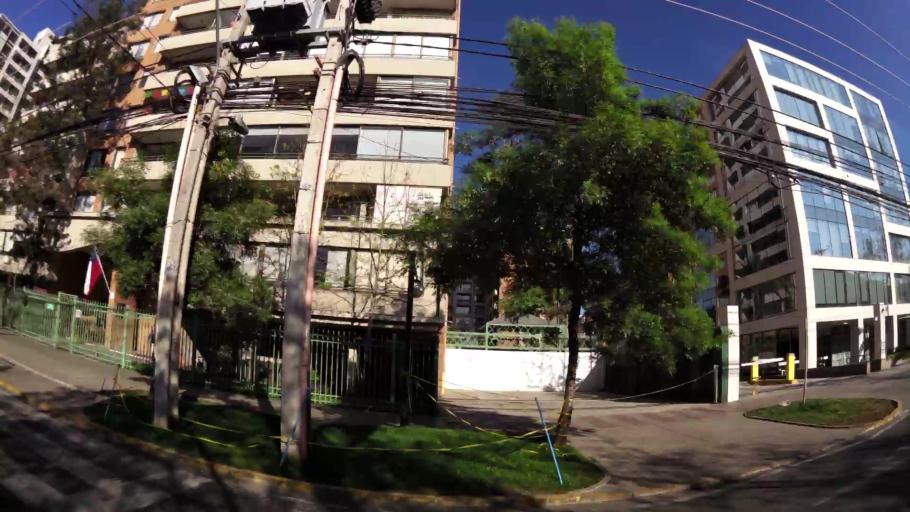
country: CL
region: Santiago Metropolitan
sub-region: Provincia de Santiago
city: Villa Presidente Frei, Nunoa, Santiago, Chile
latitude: -33.4541
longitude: -70.5920
